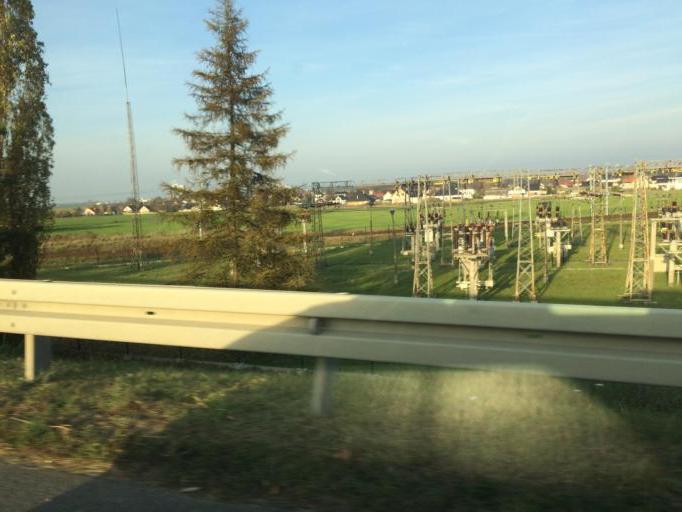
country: PL
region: Opole Voivodeship
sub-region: Powiat strzelecki
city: Strzelce Opolskie
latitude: 50.5214
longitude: 18.2794
